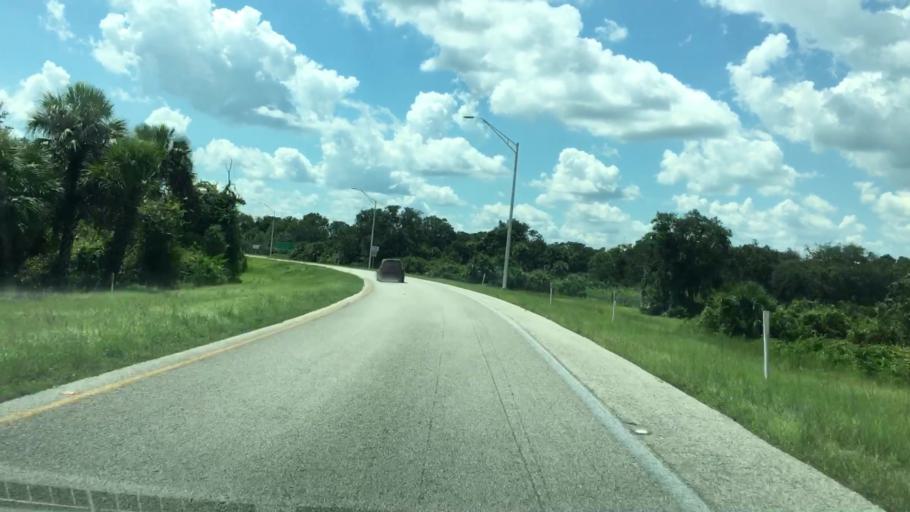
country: US
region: Florida
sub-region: Brevard County
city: South Patrick Shores
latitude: 28.1949
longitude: -80.7108
